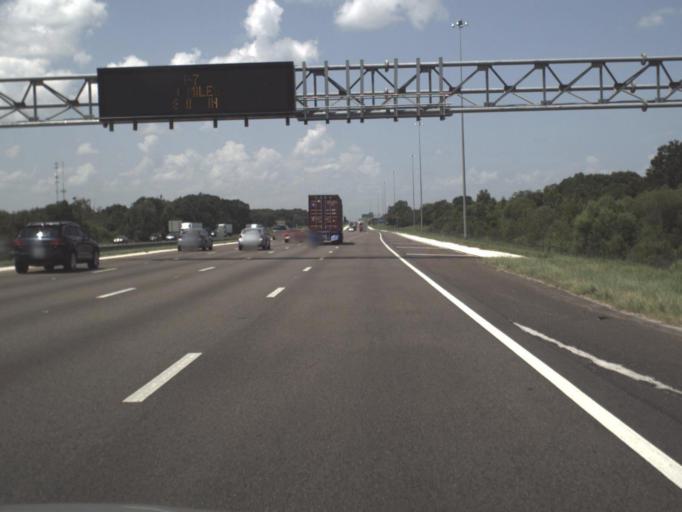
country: US
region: Florida
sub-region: Hillsborough County
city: Plant City
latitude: 28.0273
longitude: -82.1671
